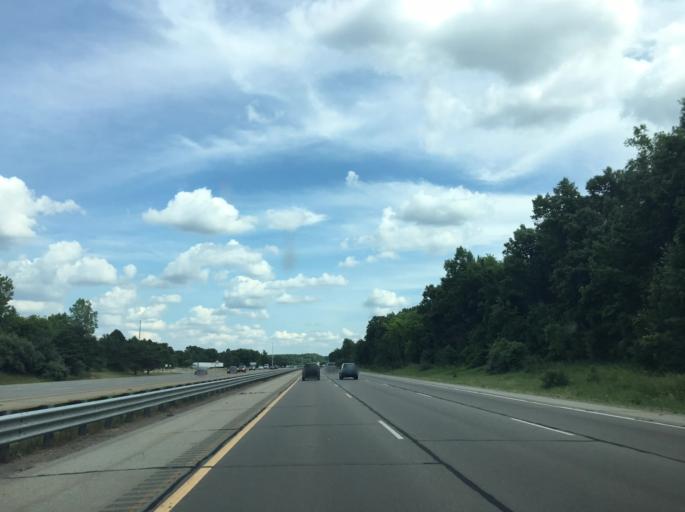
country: US
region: Michigan
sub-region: Oakland County
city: Clarkston
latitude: 42.7652
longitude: -83.5149
